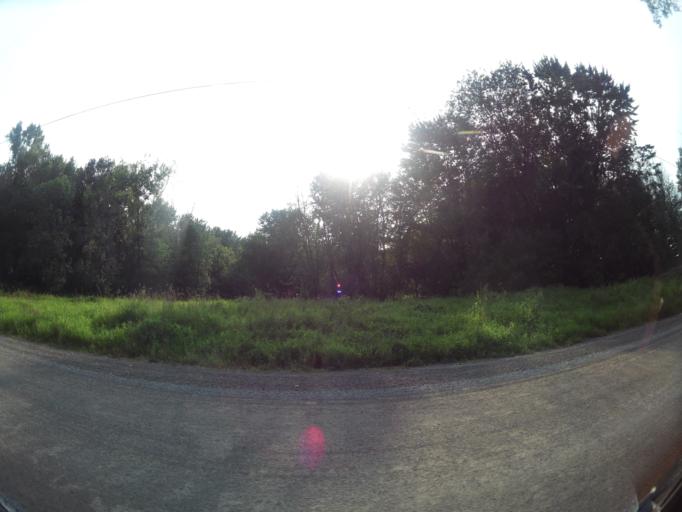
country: CA
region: Ontario
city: Clarence-Rockland
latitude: 45.5039
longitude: -75.4873
